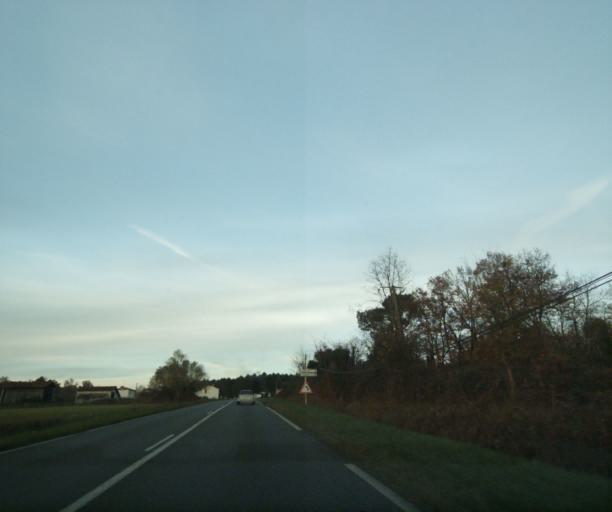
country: FR
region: Aquitaine
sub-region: Departement de la Gironde
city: Bazas
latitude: 44.4730
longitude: -0.2280
